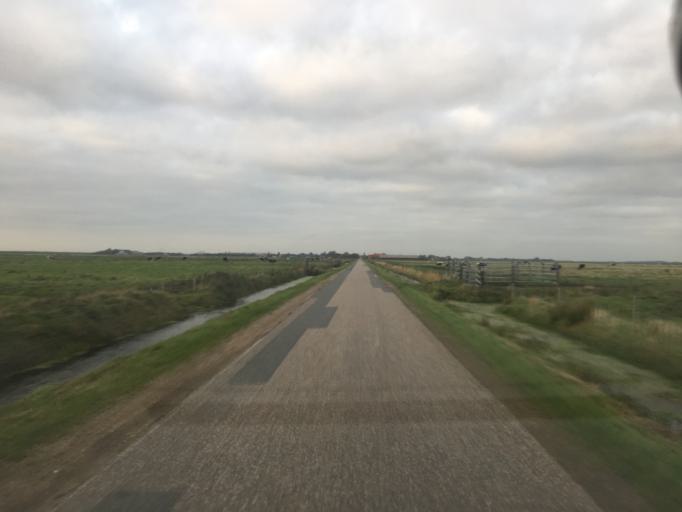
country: DE
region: Schleswig-Holstein
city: Klanxbull
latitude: 54.9409
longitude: 8.6859
